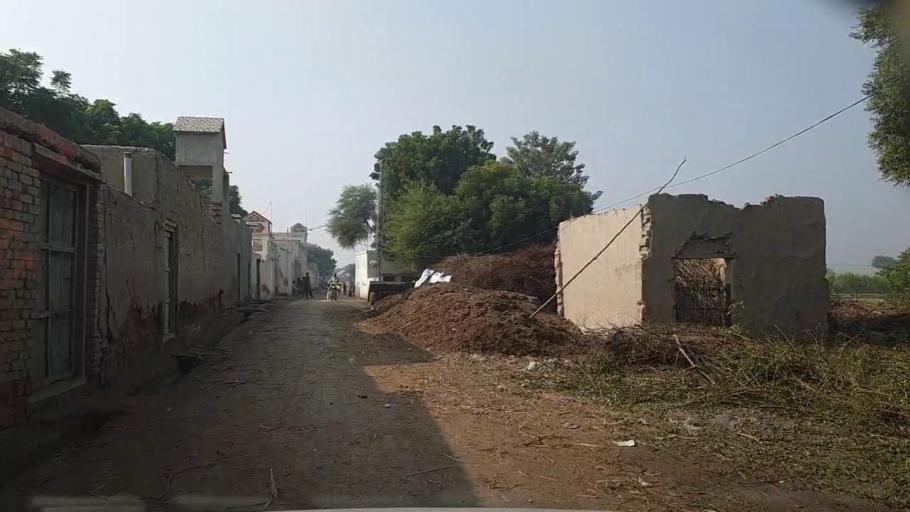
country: PK
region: Sindh
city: Setharja Old
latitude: 27.1189
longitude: 68.5126
